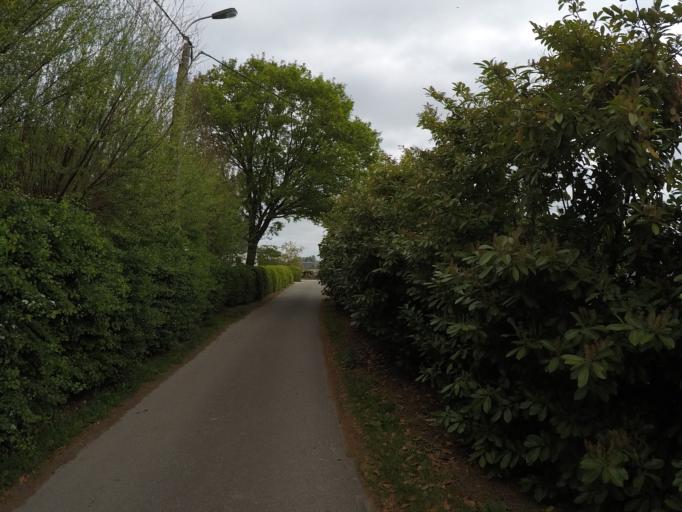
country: BE
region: Flanders
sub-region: Provincie Antwerpen
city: Ranst
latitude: 51.1769
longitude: 4.5488
